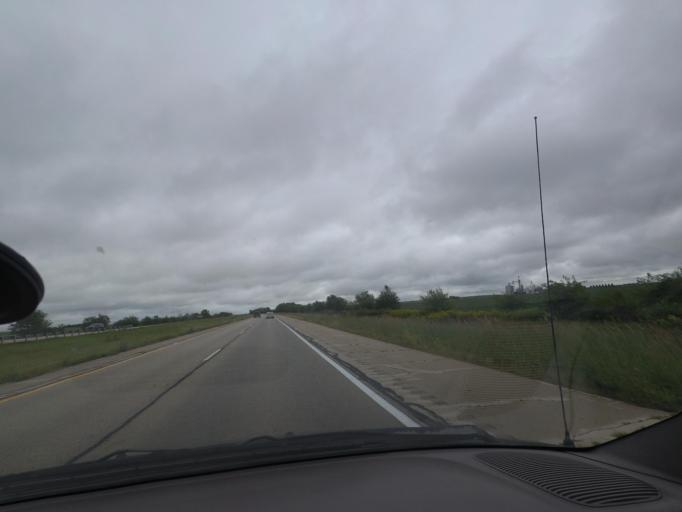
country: US
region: Illinois
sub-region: Piatt County
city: Cerro Gordo
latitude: 40.0184
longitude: -88.7216
